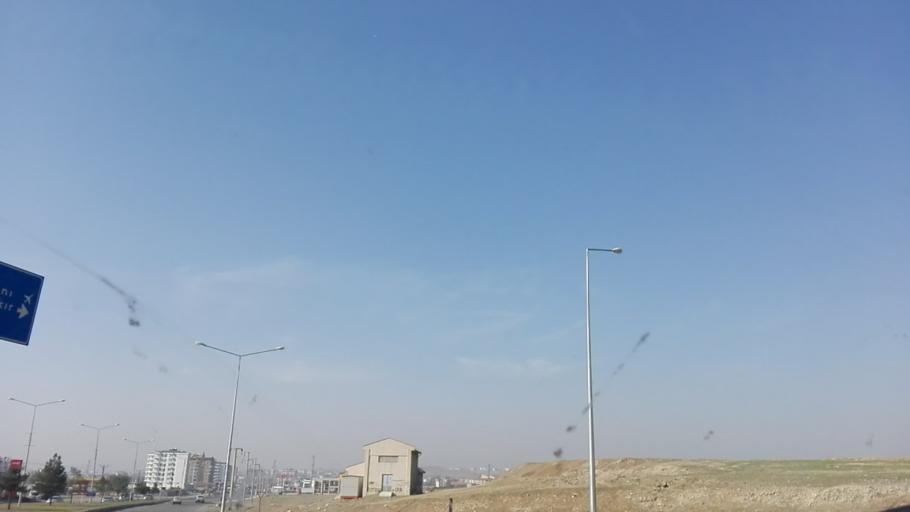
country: TR
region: Batman
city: Aydinkonak
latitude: 37.8745
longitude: 41.1744
